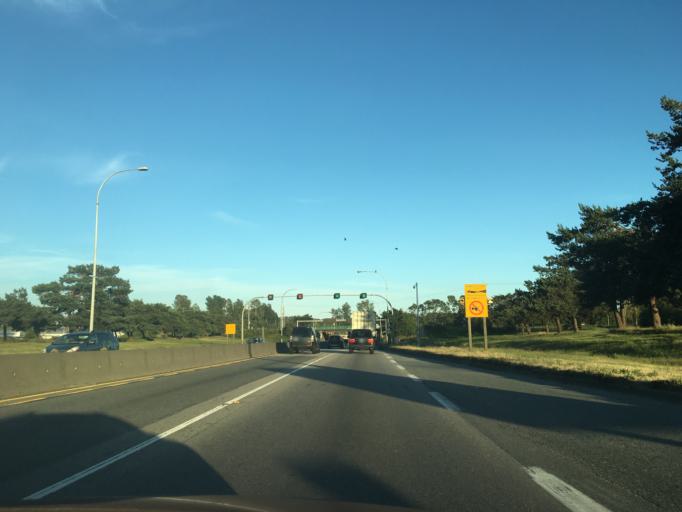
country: CA
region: British Columbia
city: Ladner
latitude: 49.1274
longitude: -123.0826
